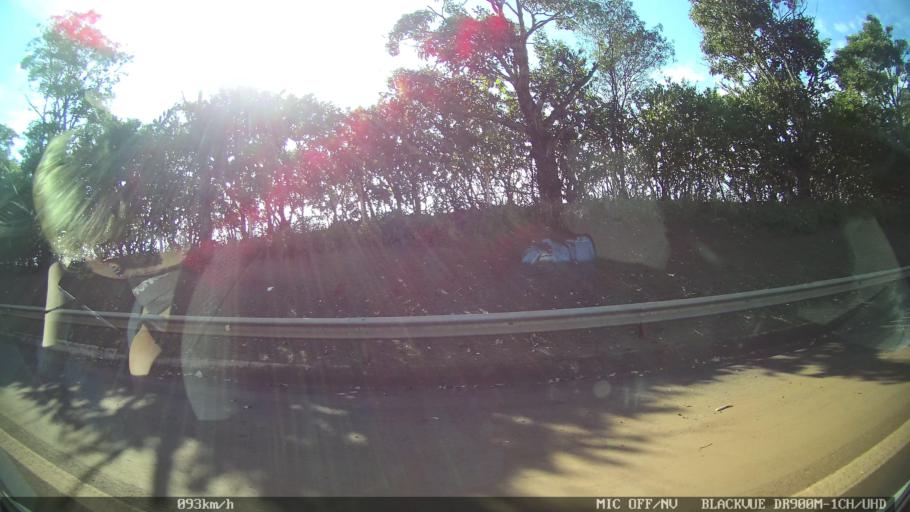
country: BR
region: Sao Paulo
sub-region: Iracemapolis
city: Iracemapolis
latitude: -22.6691
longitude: -47.5501
